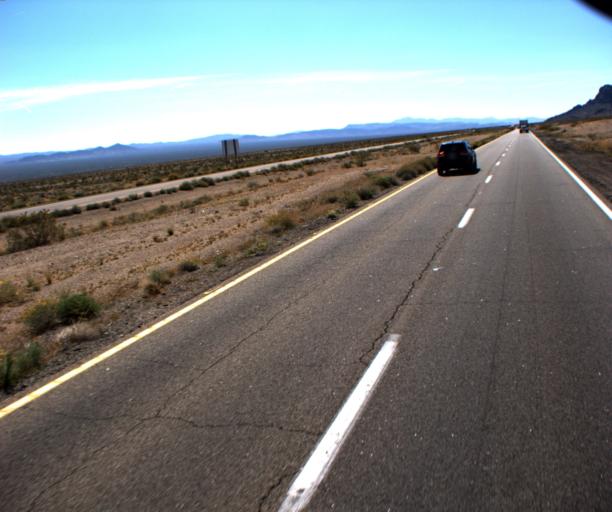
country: US
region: Nevada
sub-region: Clark County
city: Boulder City
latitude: 35.8252
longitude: -114.5574
